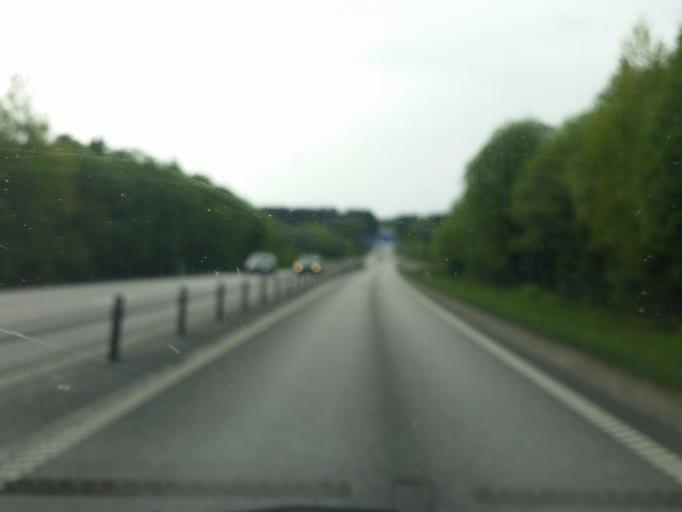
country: SE
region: Vaestra Goetaland
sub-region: Ulricehamns Kommun
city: Ulricehamn
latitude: 57.7963
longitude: 13.5421
